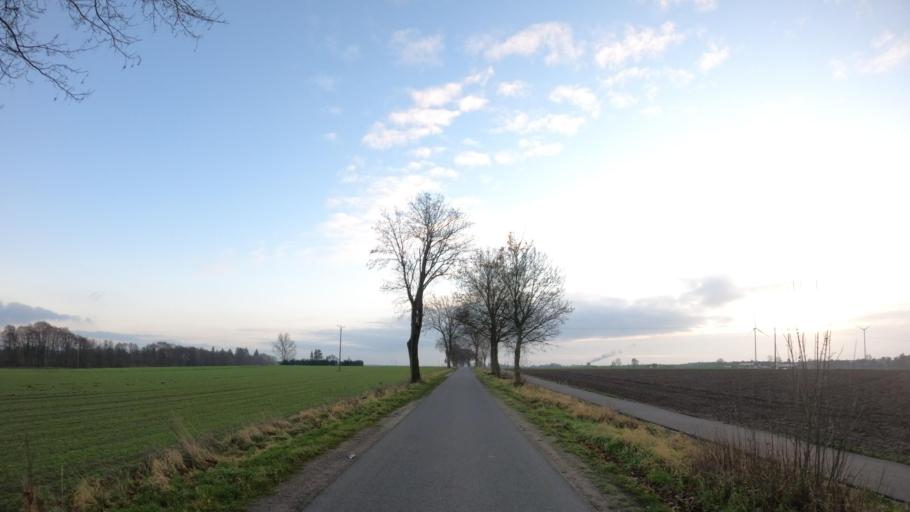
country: PL
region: West Pomeranian Voivodeship
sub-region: Powiat bialogardzki
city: Karlino
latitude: 54.1007
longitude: 15.8854
